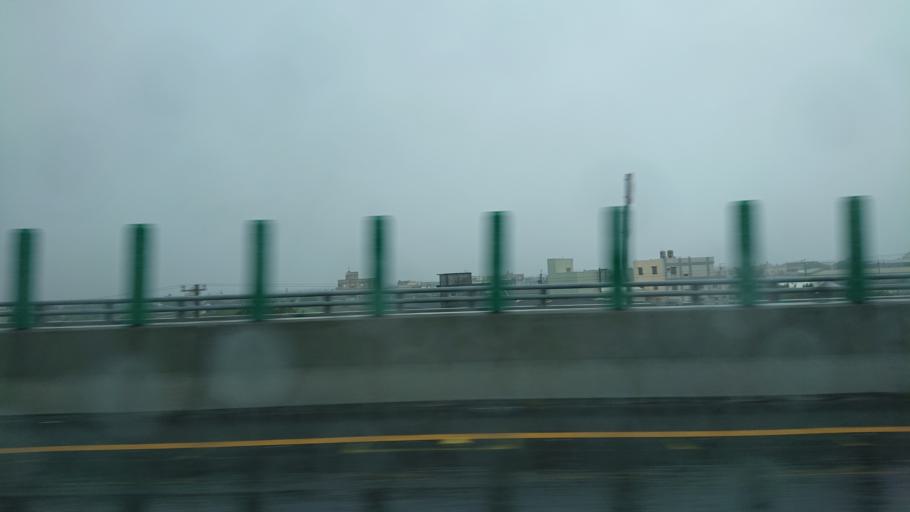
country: TW
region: Taiwan
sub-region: Changhua
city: Chang-hua
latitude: 23.9456
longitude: 120.3258
